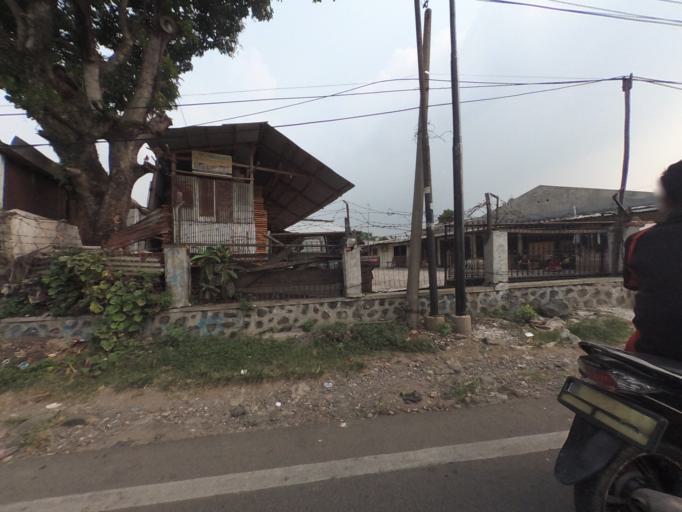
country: ID
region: West Java
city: Ciampea
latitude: -6.5650
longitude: 106.6752
